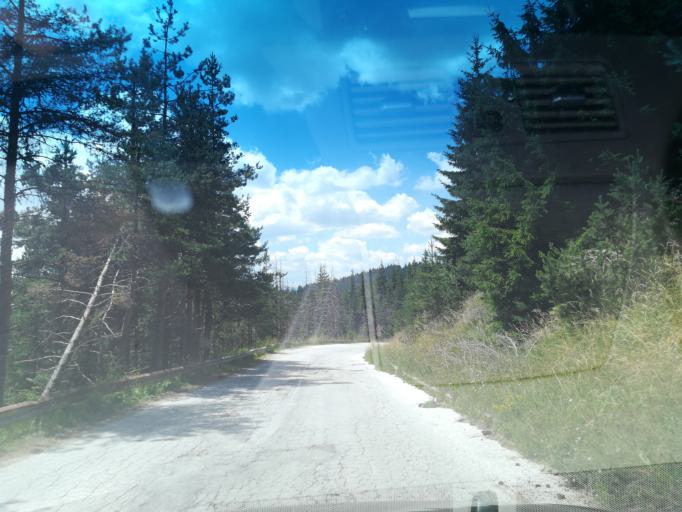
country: BG
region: Smolyan
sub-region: Obshtina Chepelare
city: Chepelare
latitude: 41.6924
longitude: 24.7657
